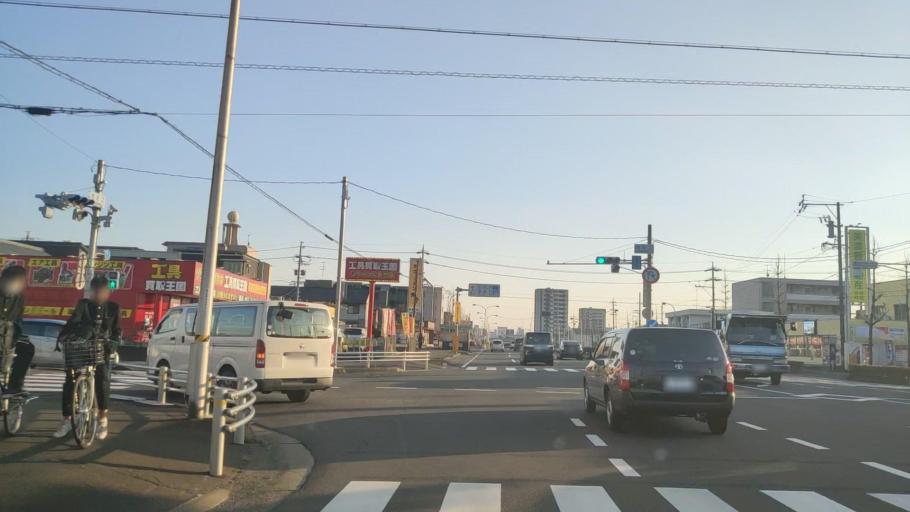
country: JP
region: Gifu
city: Gifu-shi
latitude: 35.4088
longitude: 136.7271
